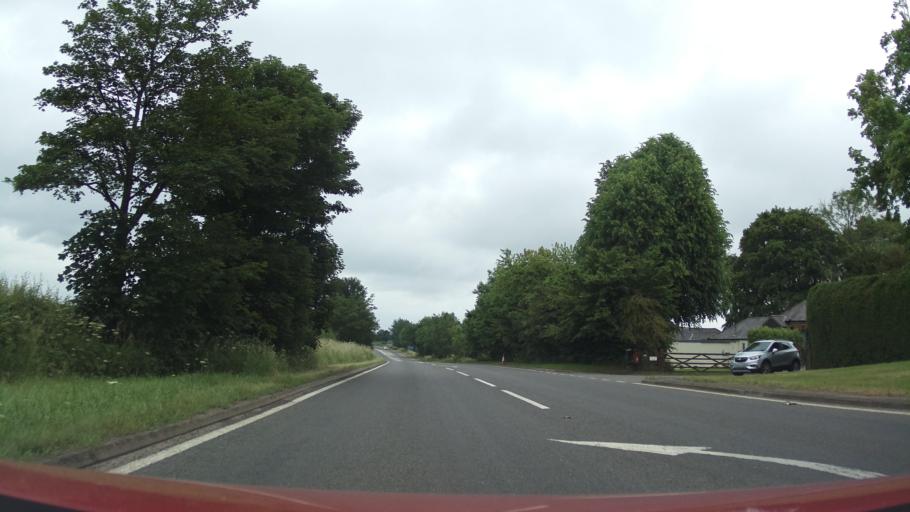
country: GB
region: England
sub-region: District of Rutland
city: Ridlington
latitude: 52.5984
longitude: -0.8677
